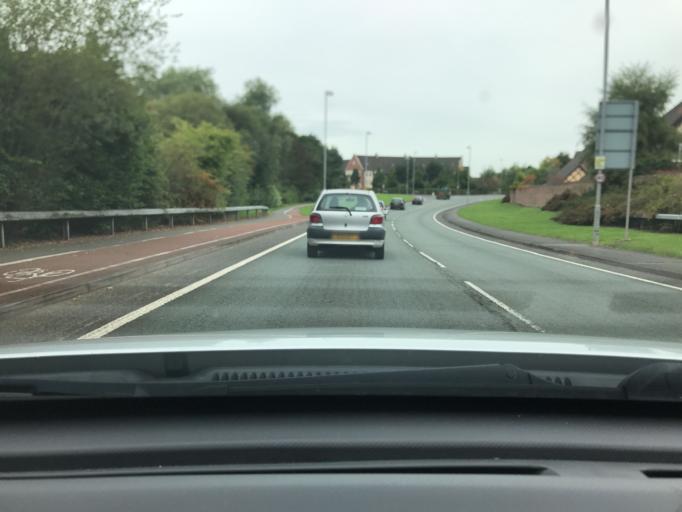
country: GB
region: England
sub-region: Cheshire West and Chester
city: Northwich
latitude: 53.2434
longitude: -2.5181
